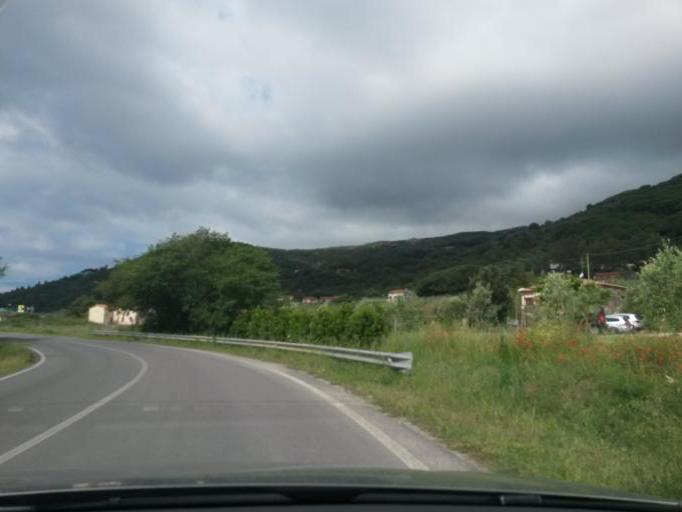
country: IT
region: Tuscany
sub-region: Provincia di Livorno
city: Campo nell'Elba
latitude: 42.7444
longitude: 10.2196
